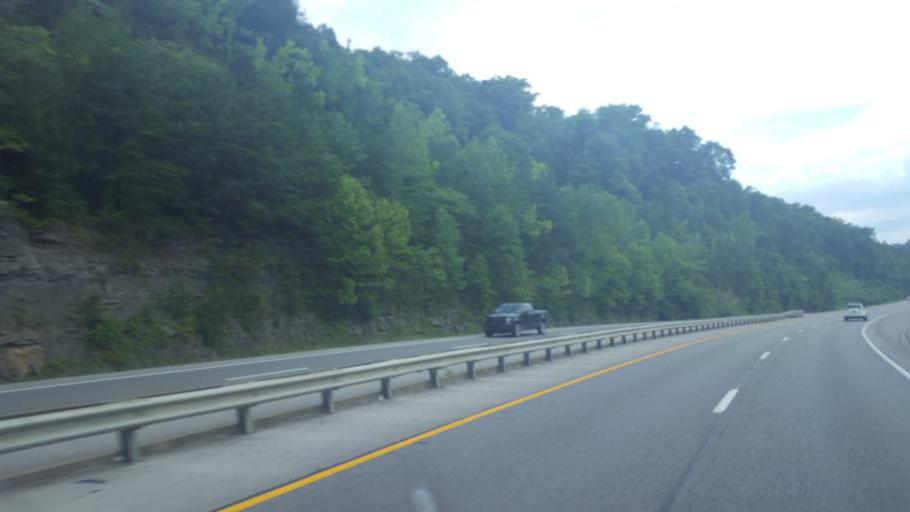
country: US
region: Kentucky
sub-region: Pike County
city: Pikeville
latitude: 37.4581
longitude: -82.5175
